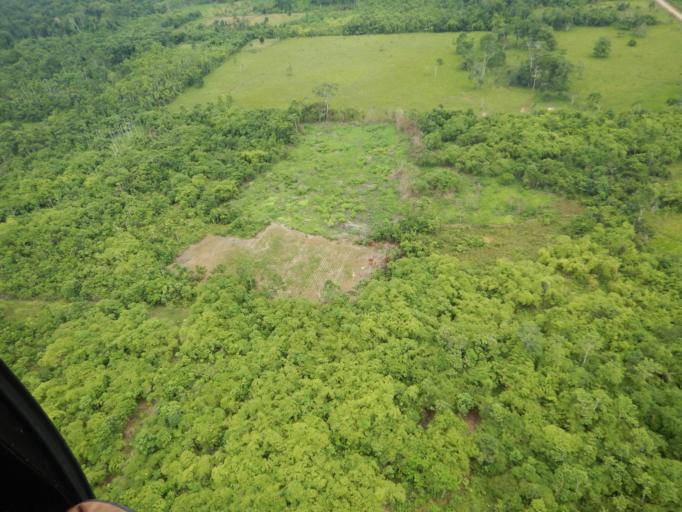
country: BO
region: Cochabamba
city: Chimore
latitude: -16.9873
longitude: -64.9501
